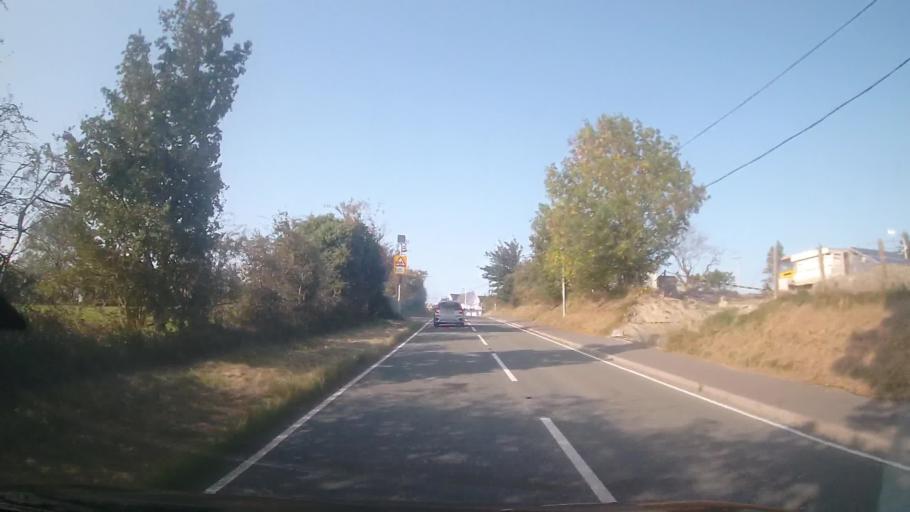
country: GB
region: Wales
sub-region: County of Ceredigion
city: Lledrod
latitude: 52.2869
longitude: -3.8608
